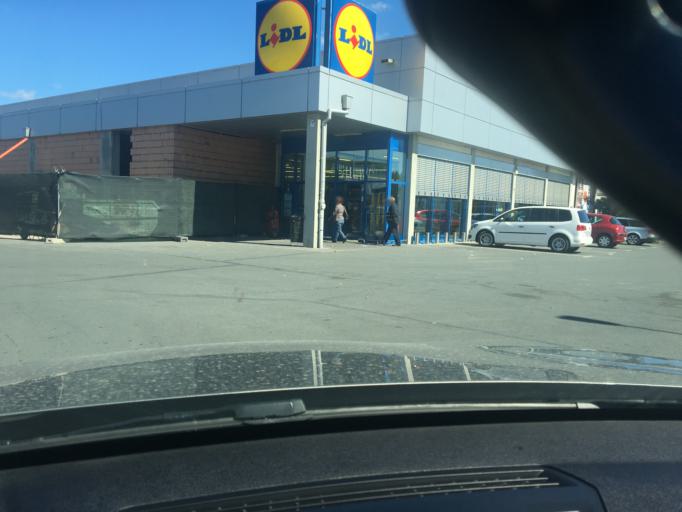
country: BG
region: Burgas
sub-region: Obshtina Burgas
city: Burgas
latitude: 42.5315
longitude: 27.4623
